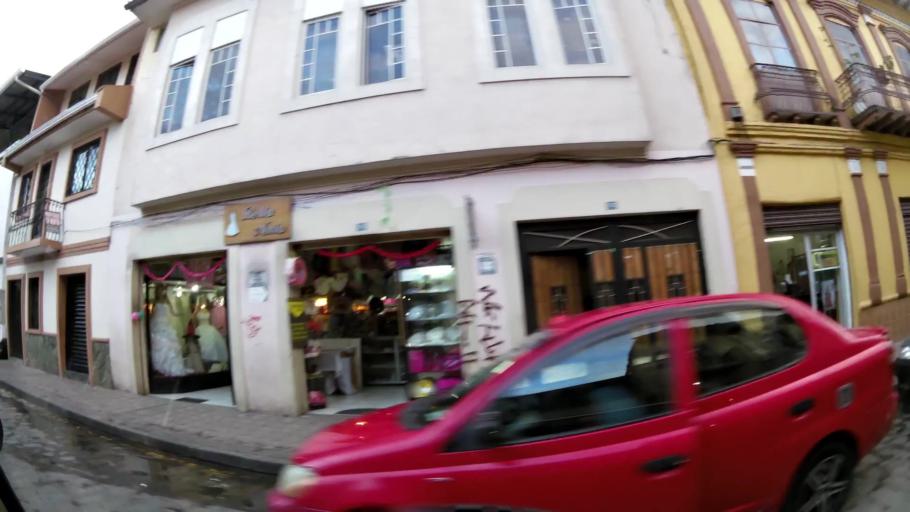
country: EC
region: Azuay
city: Cuenca
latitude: -2.8969
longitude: -79.0089
